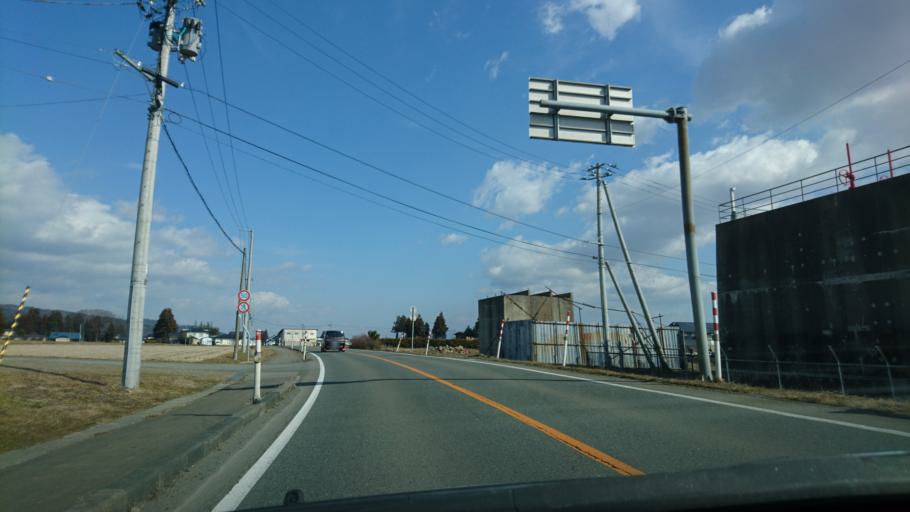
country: JP
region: Iwate
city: Morioka-shi
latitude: 39.5614
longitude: 141.1083
